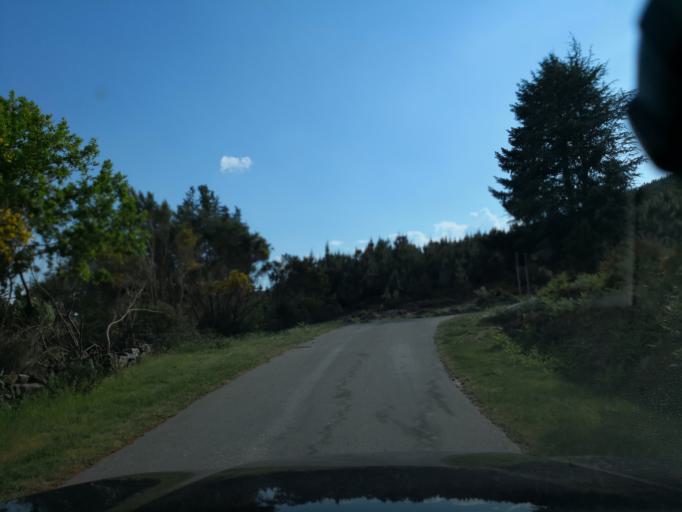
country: PT
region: Vila Real
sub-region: Vila Real
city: Vila Real
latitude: 41.3603
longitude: -7.7377
